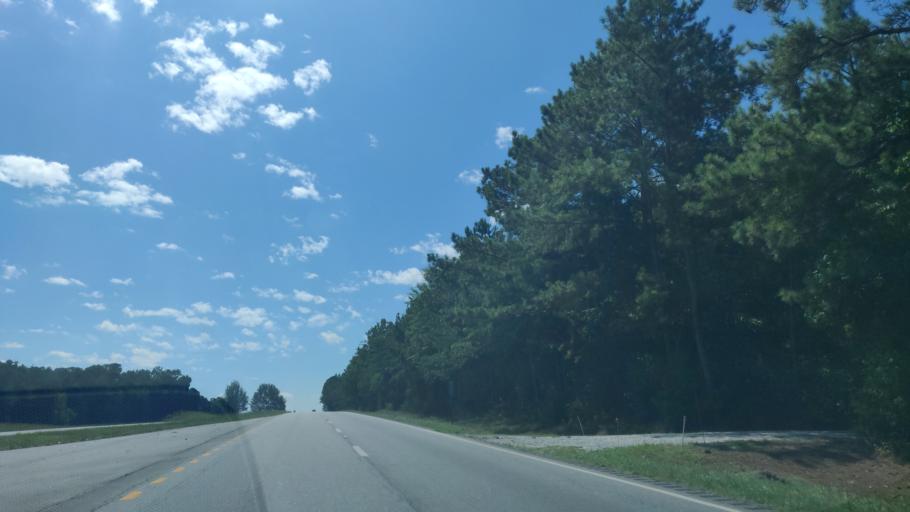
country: US
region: Alabama
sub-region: Lee County
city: Smiths Station
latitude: 32.5926
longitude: -85.1969
